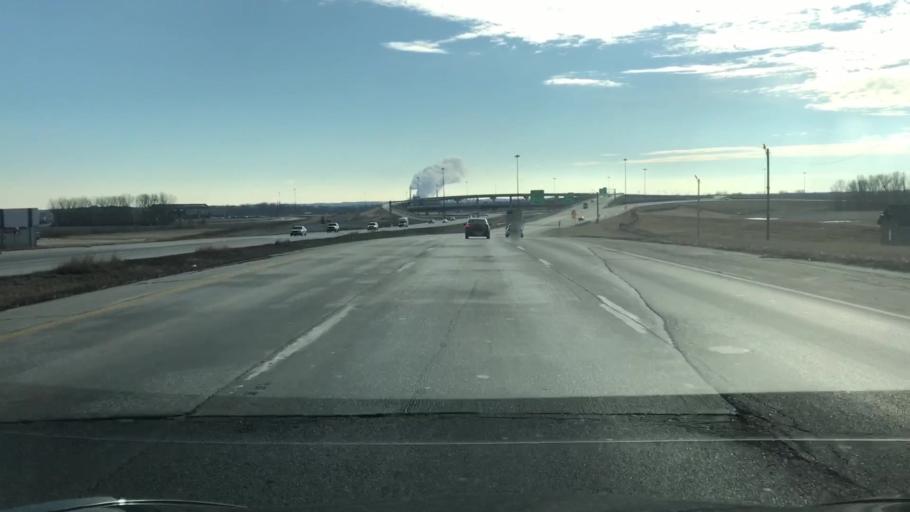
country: US
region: Nebraska
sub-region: Douglas County
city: Omaha
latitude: 41.2407
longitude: -95.9037
